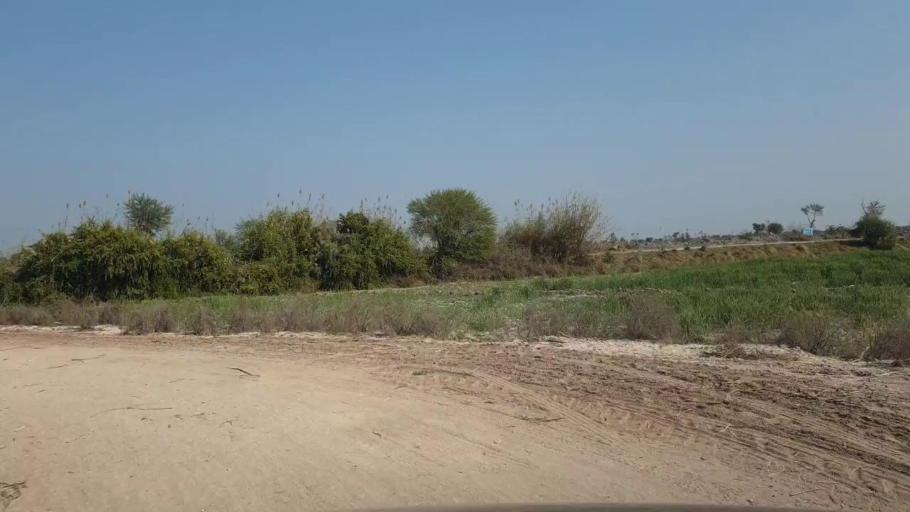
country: PK
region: Sindh
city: Shahdadpur
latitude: 25.9497
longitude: 68.4778
